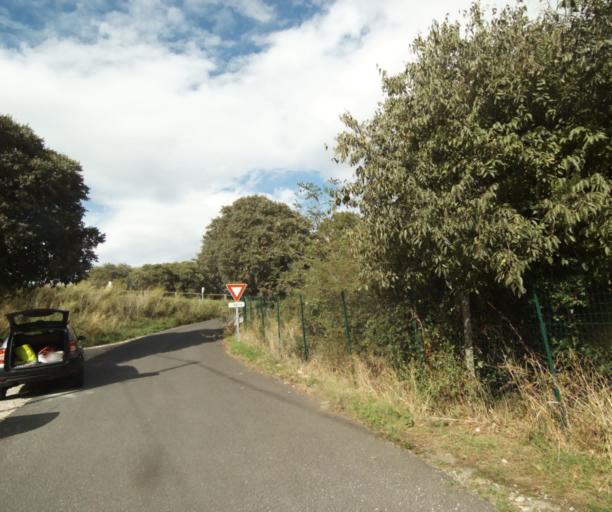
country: FR
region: Languedoc-Roussillon
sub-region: Departement des Pyrenees-Orientales
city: Sant Andreu de Sureda
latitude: 42.5322
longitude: 2.9887
